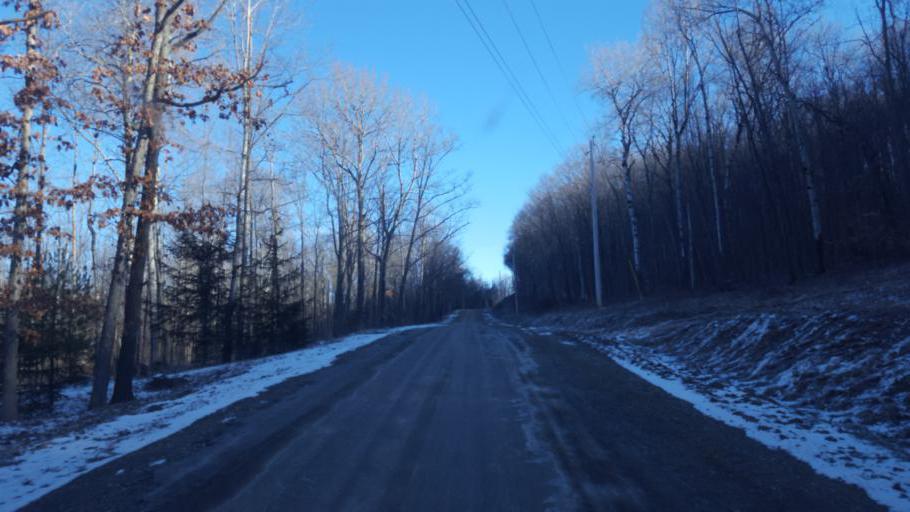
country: US
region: New York
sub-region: Allegany County
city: Wellsville
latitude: 42.1546
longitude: -77.9102
